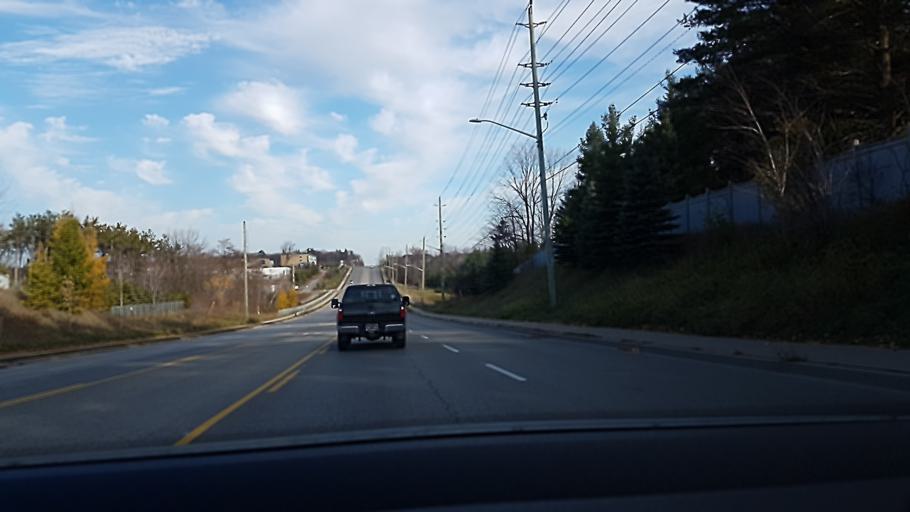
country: CA
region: Ontario
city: Barrie
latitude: 44.3608
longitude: -79.6307
